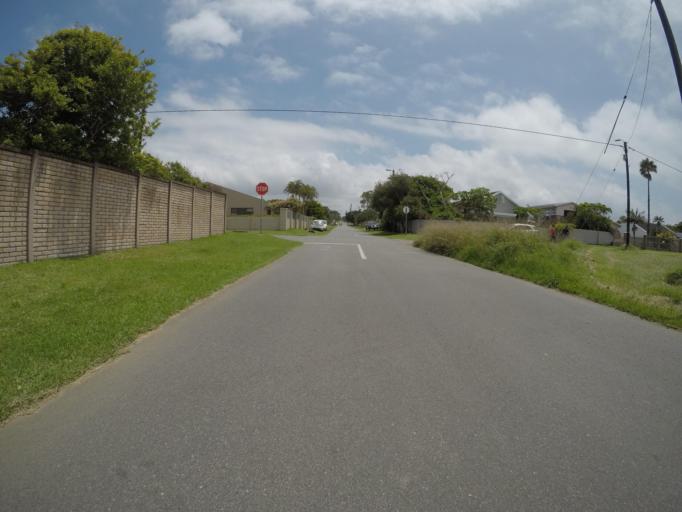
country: ZA
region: Eastern Cape
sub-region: Buffalo City Metropolitan Municipality
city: East London
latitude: -32.9462
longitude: 28.0147
